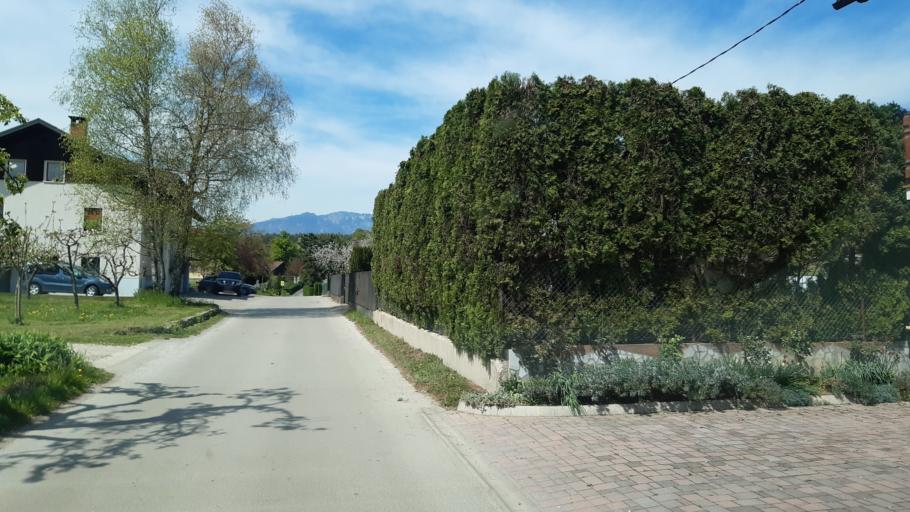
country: SI
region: Domzale
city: Radomlje
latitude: 46.1785
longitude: 14.6337
